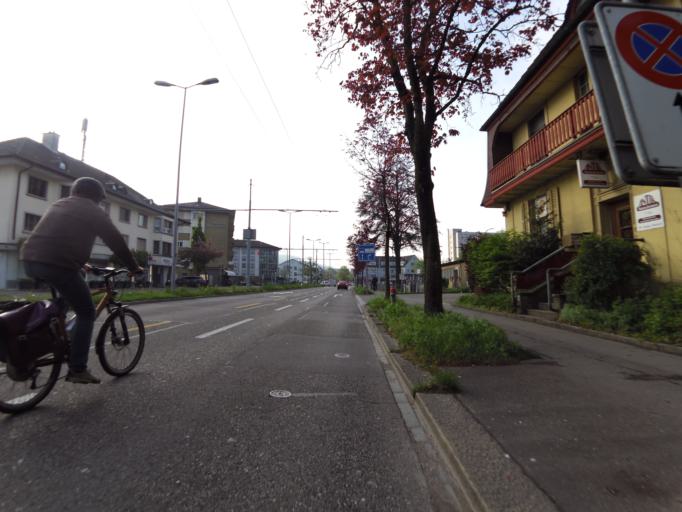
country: CH
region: Zurich
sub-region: Bezirk Zuerich
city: Zuerich (Kreis 6) / Unterstrass
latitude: 47.4033
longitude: 8.5345
